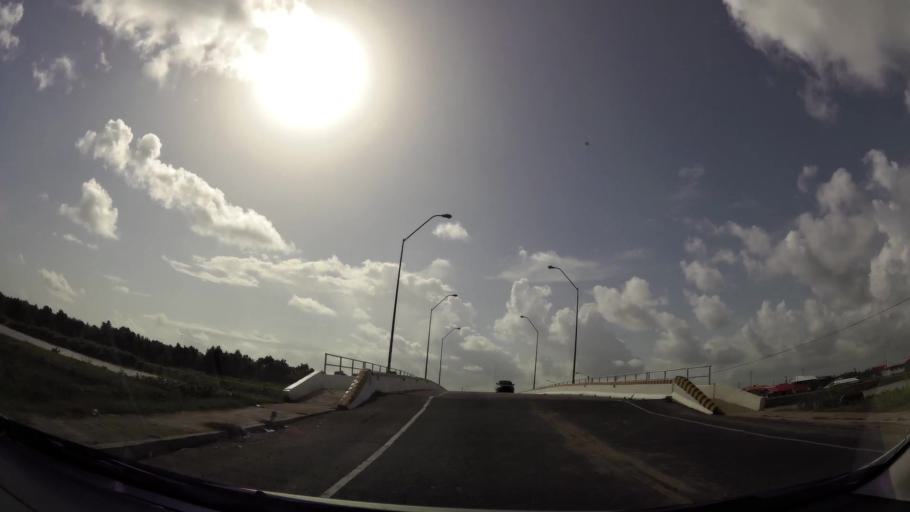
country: GY
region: Demerara-Mahaica
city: Mahaica Village
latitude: 6.7384
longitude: -57.9537
